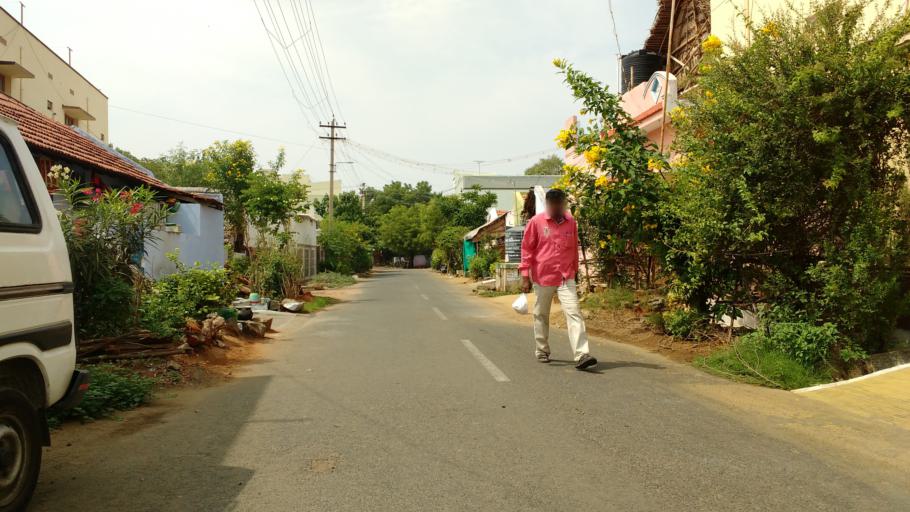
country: IN
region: Tamil Nadu
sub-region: Erode
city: Gobichettipalayam
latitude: 11.4531
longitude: 77.4451
